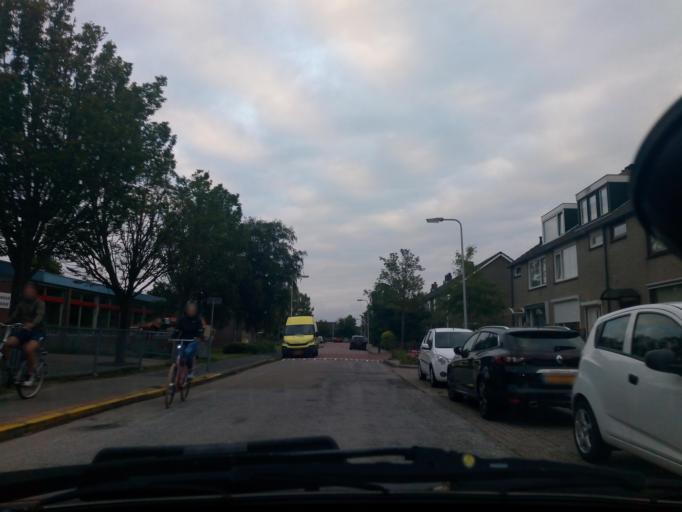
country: NL
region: South Holland
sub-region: Gemeente Alphen aan den Rijn
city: Alphen aan den Rijn
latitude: 52.1666
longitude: 4.7038
